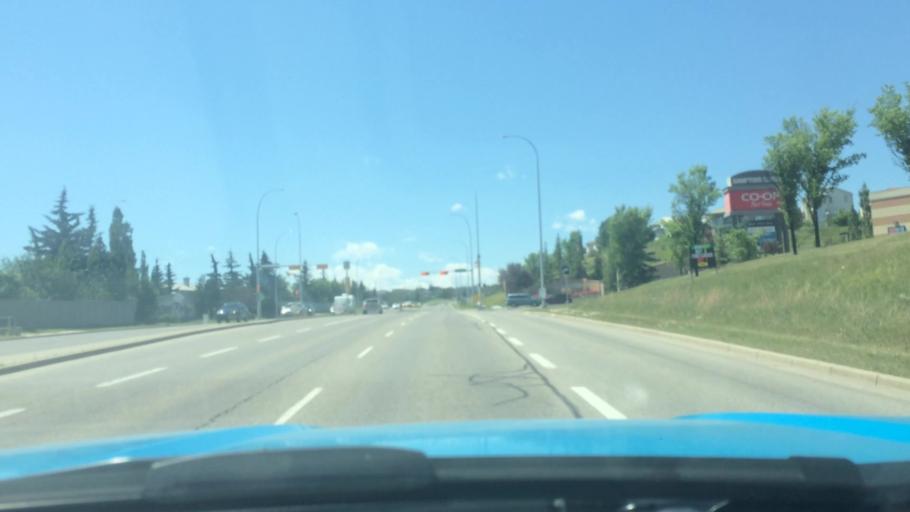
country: CA
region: Alberta
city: Calgary
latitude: 51.1408
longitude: -114.1306
